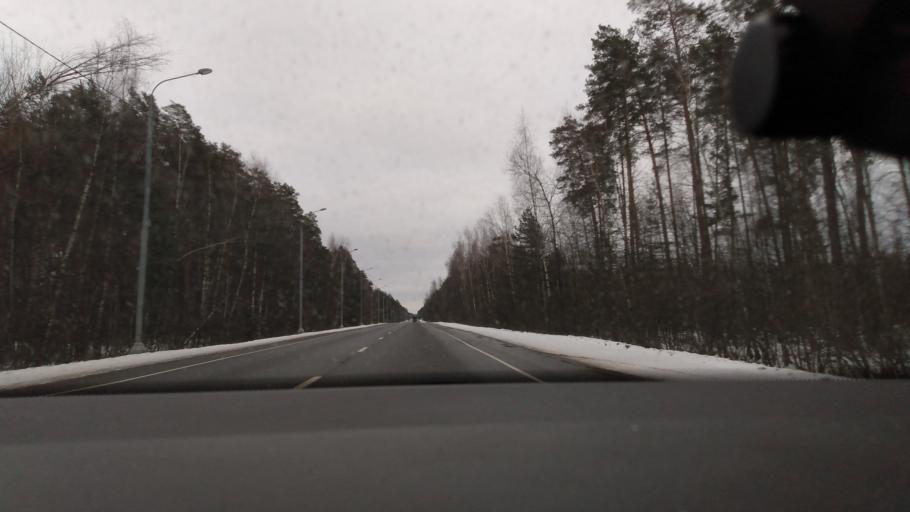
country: RU
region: Moskovskaya
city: Il'inskiy Pogost
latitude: 55.4651
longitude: 38.9737
